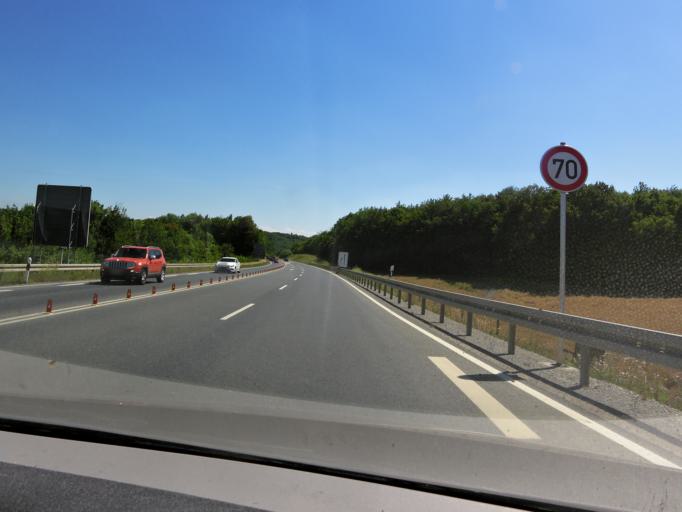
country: DE
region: Bavaria
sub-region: Regierungsbezirk Unterfranken
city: Reichenberg
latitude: 49.7493
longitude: 9.9270
